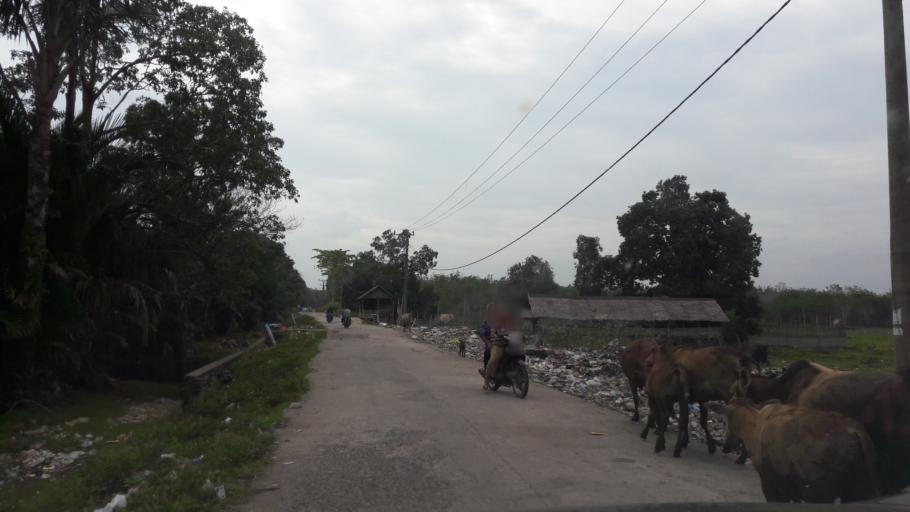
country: ID
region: South Sumatra
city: Gunungmenang
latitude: -3.1079
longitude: 104.0728
